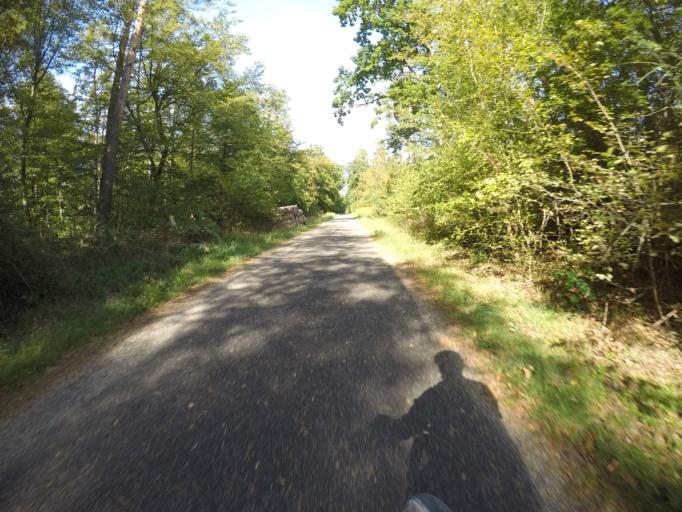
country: DE
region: Baden-Wuerttemberg
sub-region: Karlsruhe Region
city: Kronau
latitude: 49.2074
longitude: 8.6143
